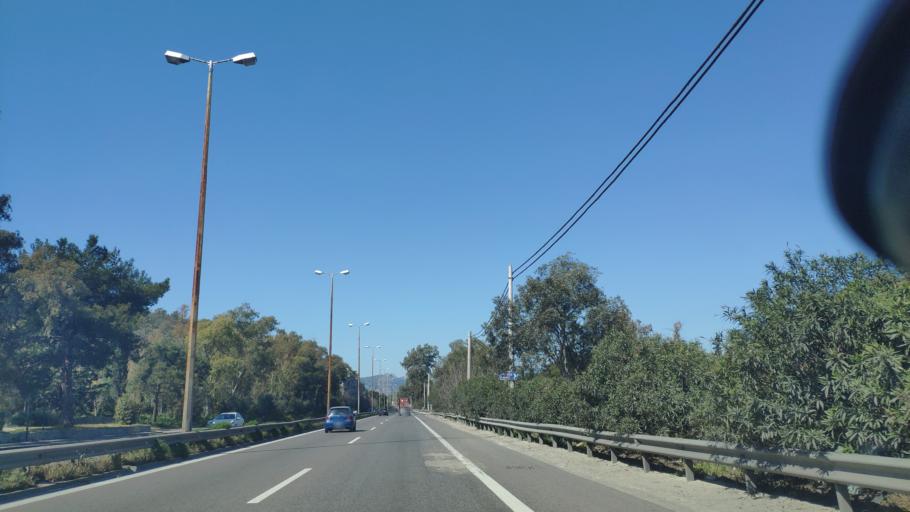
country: GR
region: Attica
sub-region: Nomarchia Athinas
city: Skaramangas
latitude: 38.0126
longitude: 23.6178
